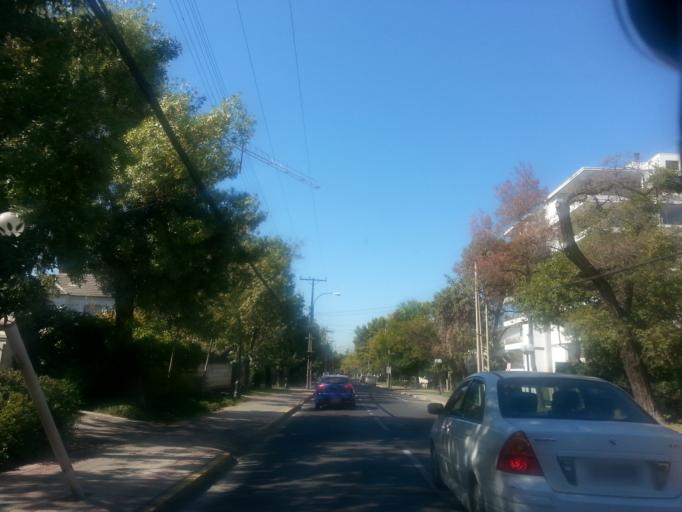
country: CL
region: Santiago Metropolitan
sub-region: Provincia de Santiago
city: Villa Presidente Frei, Nunoa, Santiago, Chile
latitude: -33.4342
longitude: -70.5960
